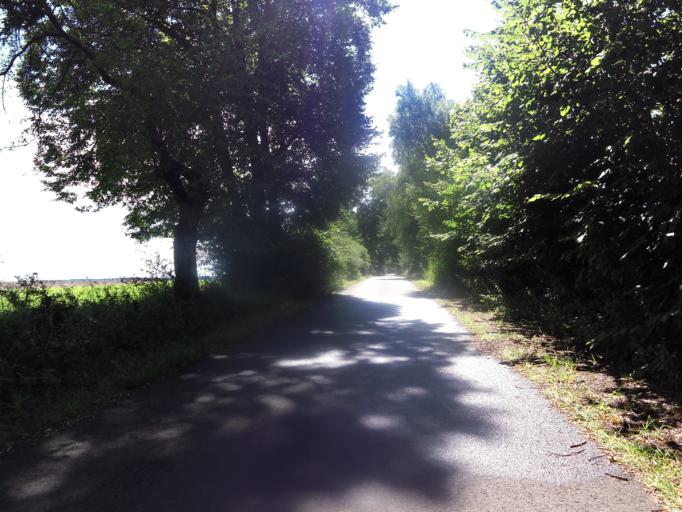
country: DE
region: Brandenburg
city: Lychen
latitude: 53.2339
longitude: 13.2872
